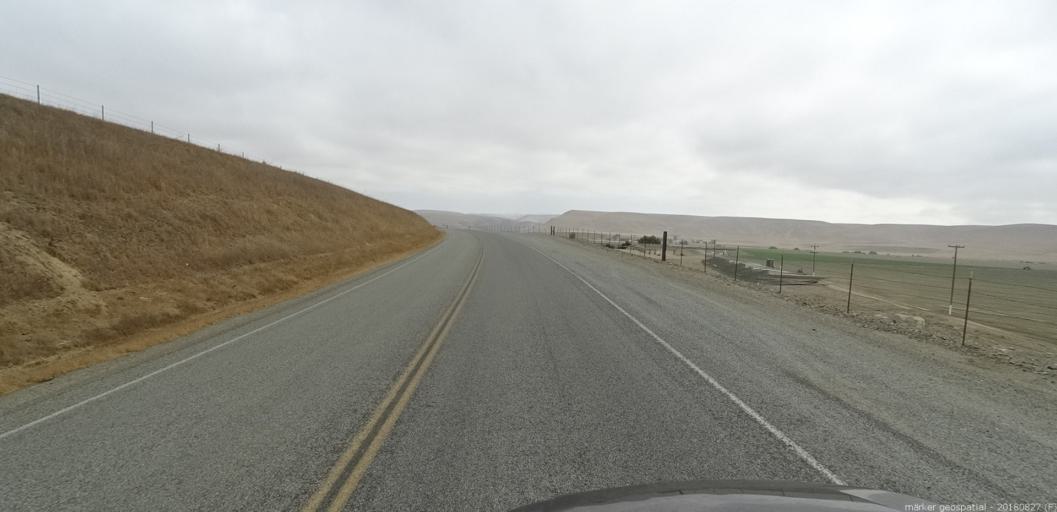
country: US
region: California
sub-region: Monterey County
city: King City
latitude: 36.2486
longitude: -121.0950
